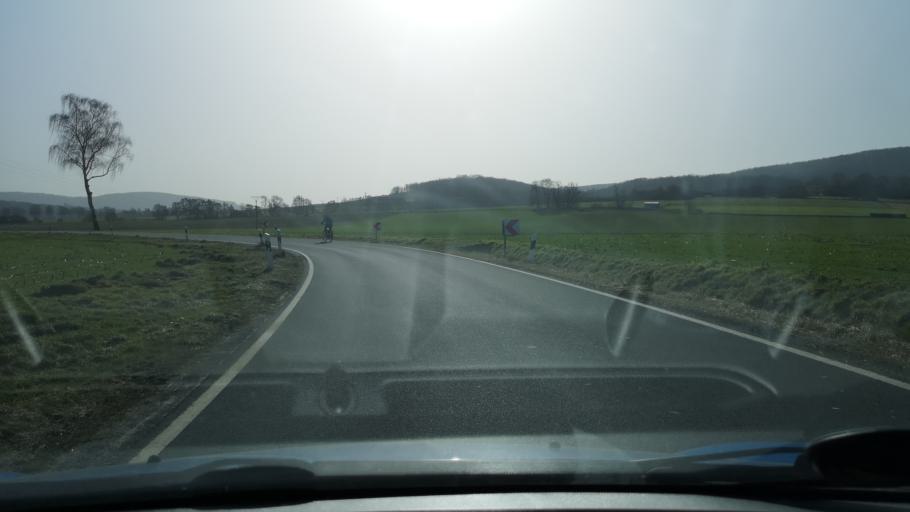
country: DE
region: Lower Saxony
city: Weenzen
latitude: 52.0030
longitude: 9.6379
